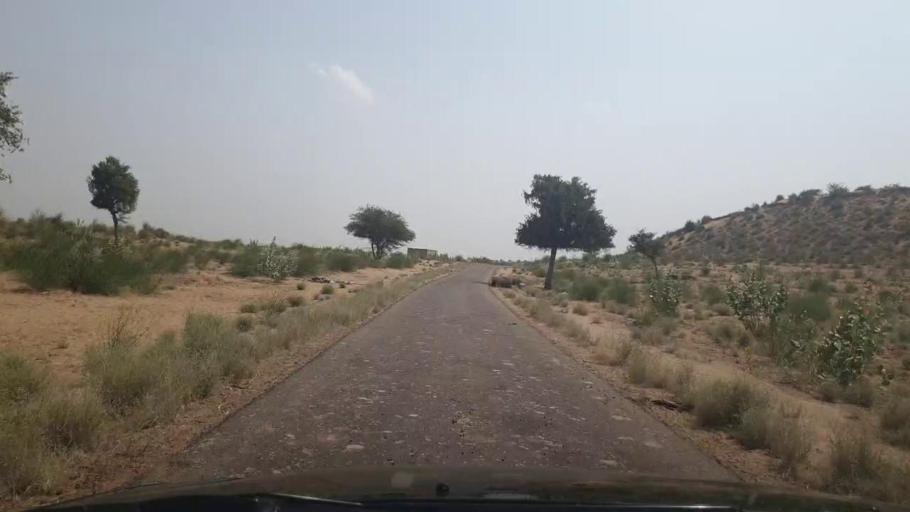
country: PK
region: Sindh
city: Islamkot
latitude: 25.0097
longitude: 70.4061
